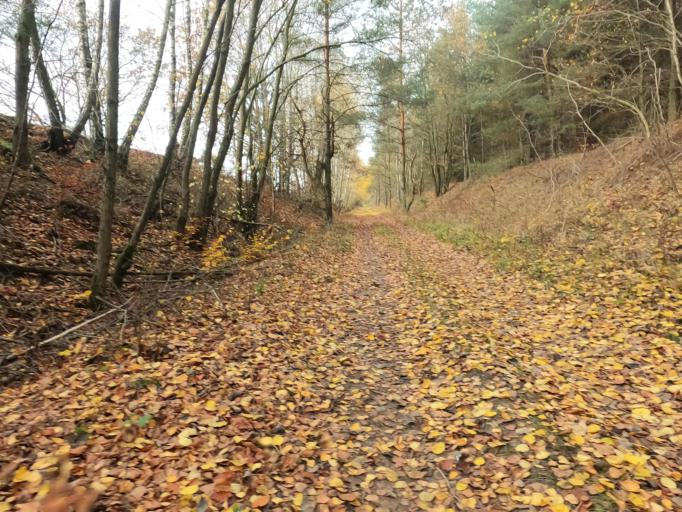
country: PL
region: Pomeranian Voivodeship
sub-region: Powiat starogardzki
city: Starogard Gdanski
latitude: 53.9924
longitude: 18.4633
